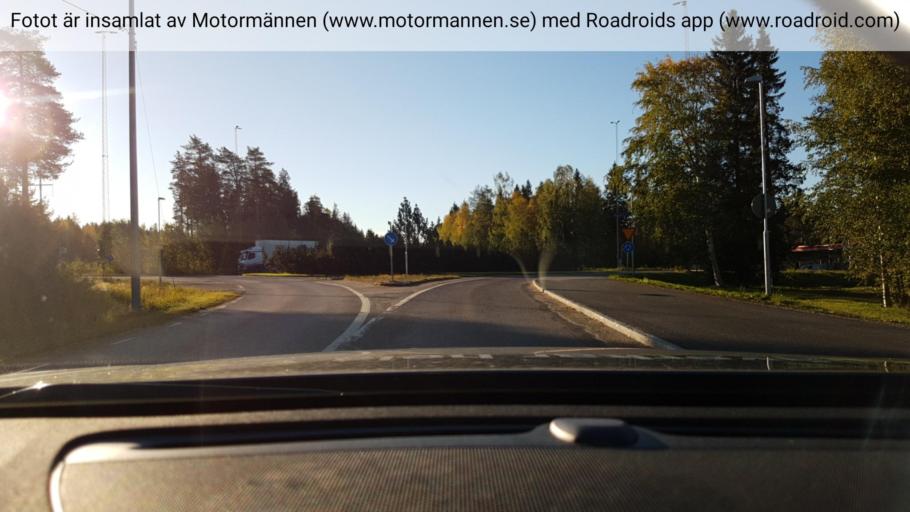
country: SE
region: Norrbotten
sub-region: Lulea Kommun
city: Gammelstad
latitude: 65.6340
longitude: 22.0319
